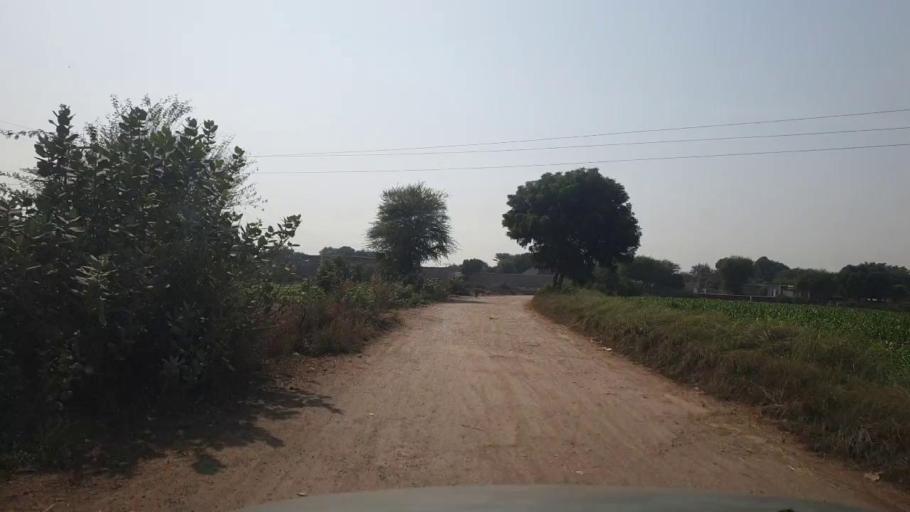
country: PK
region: Sindh
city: Bhit Shah
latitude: 25.7377
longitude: 68.5082
